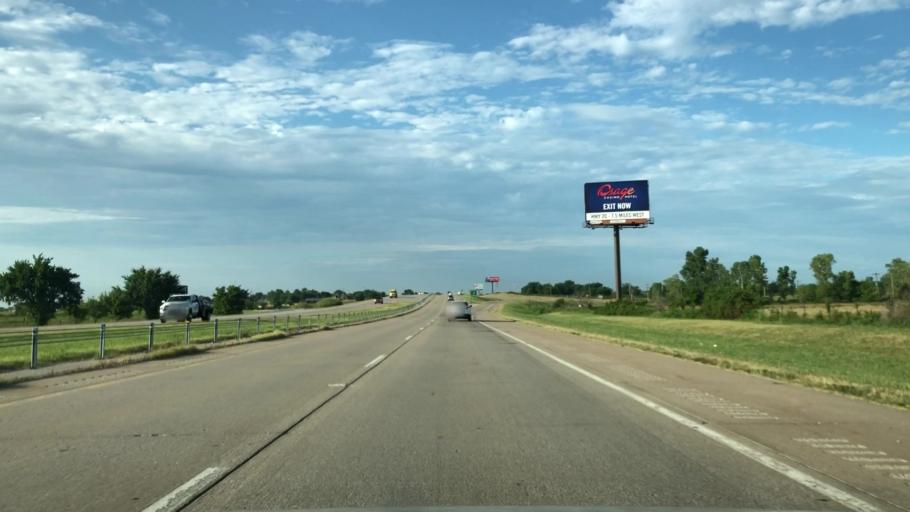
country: US
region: Oklahoma
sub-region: Osage County
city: Skiatook
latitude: 36.3704
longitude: -95.9208
